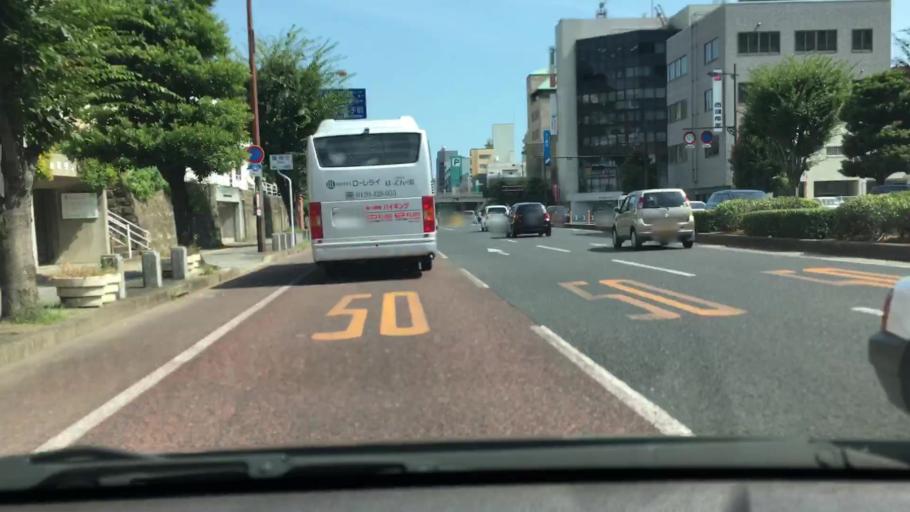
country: JP
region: Nagasaki
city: Sasebo
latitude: 33.1767
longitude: 129.7176
